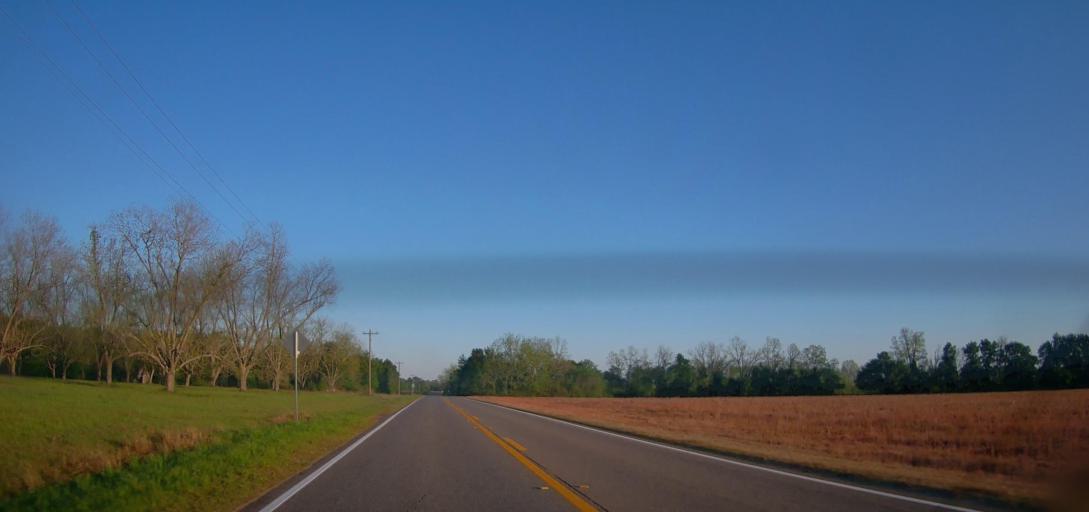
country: US
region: Georgia
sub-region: Irwin County
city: Ocilla
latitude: 31.6124
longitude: -83.2632
